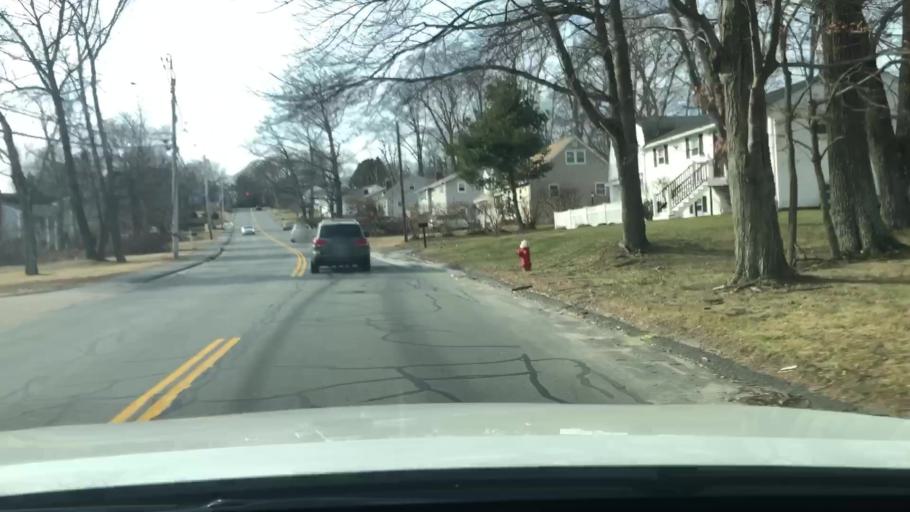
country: US
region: Massachusetts
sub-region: Worcester County
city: Hopedale
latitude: 42.1504
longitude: -71.5364
